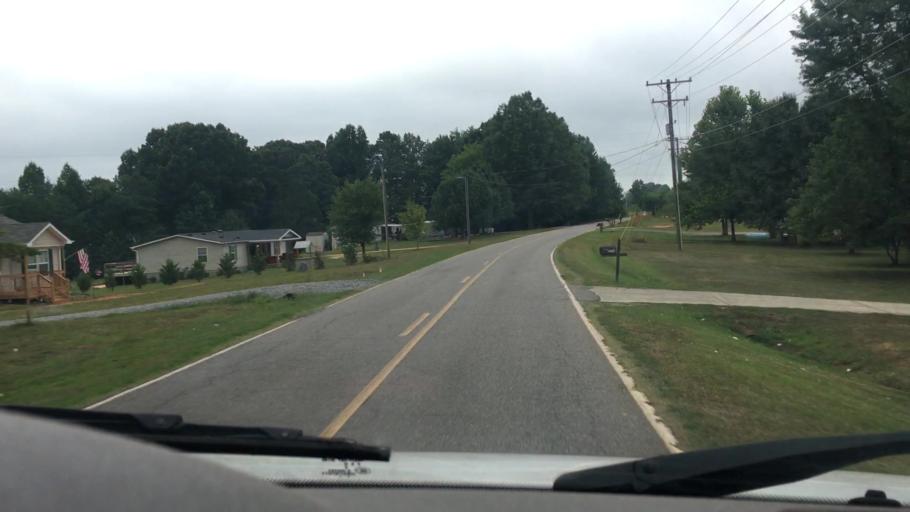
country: US
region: North Carolina
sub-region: Gaston County
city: Davidson
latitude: 35.5348
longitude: -80.8315
